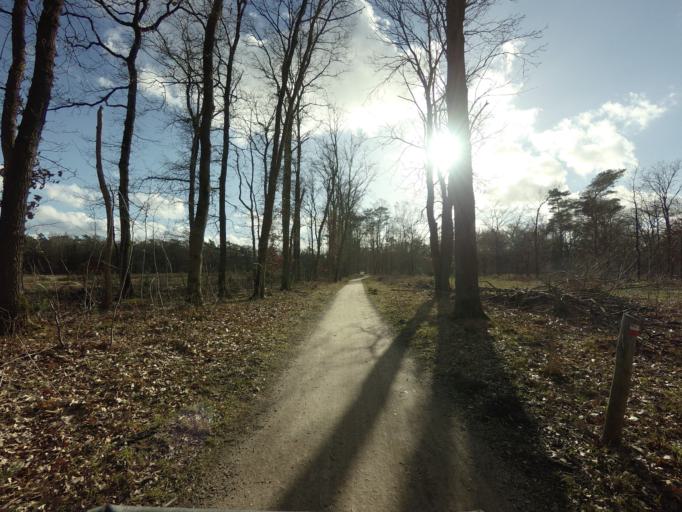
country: NL
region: North Holland
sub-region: Gemeente Bussum
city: Bussum
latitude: 52.2568
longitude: 5.1539
